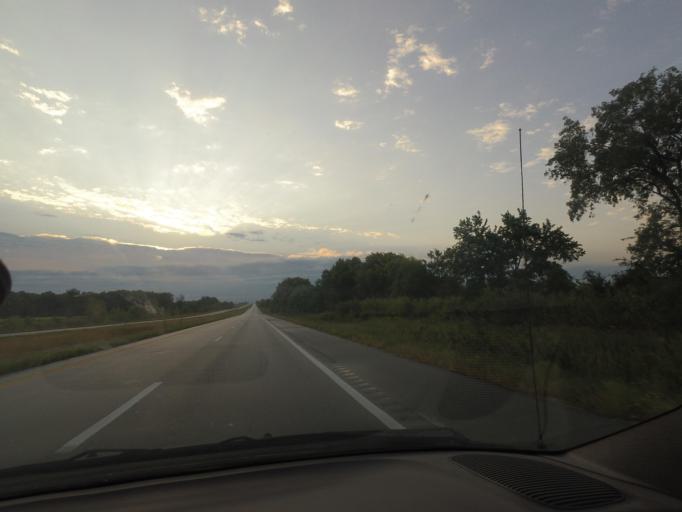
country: US
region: Missouri
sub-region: Shelby County
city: Shelbina
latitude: 39.7335
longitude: -92.2108
